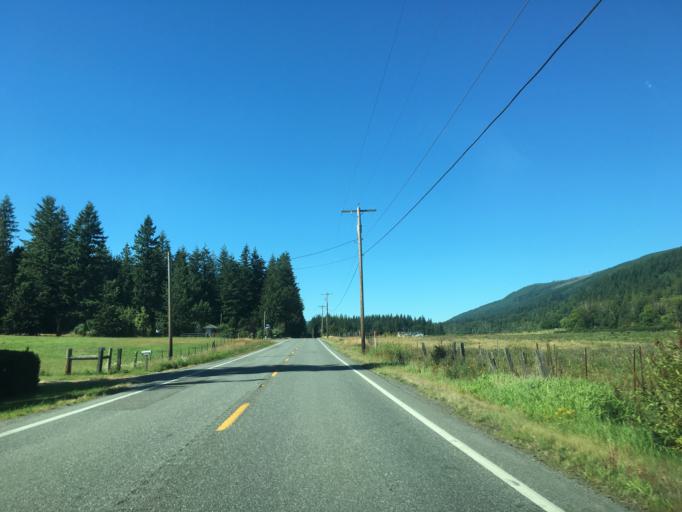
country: US
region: Washington
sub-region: Skagit County
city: Sedro-Woolley
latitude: 48.5739
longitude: -122.2245
